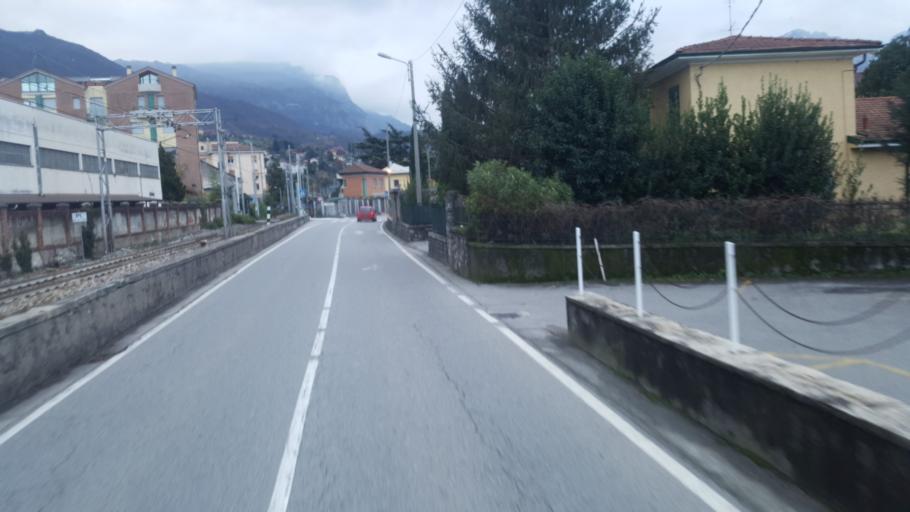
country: IT
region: Lombardy
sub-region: Provincia di Lecco
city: Mandello del Lario
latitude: 45.9177
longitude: 9.3173
